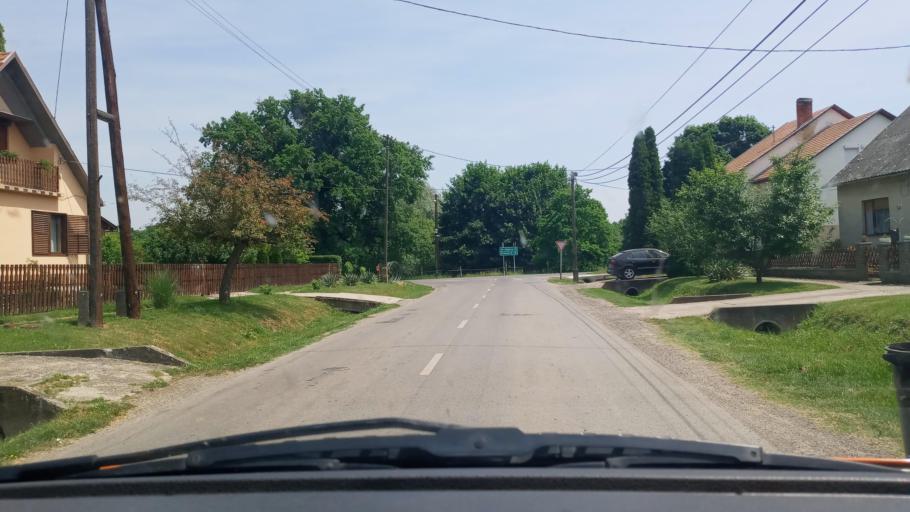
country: HU
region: Baranya
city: Szigetvar
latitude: 45.9666
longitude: 17.7221
